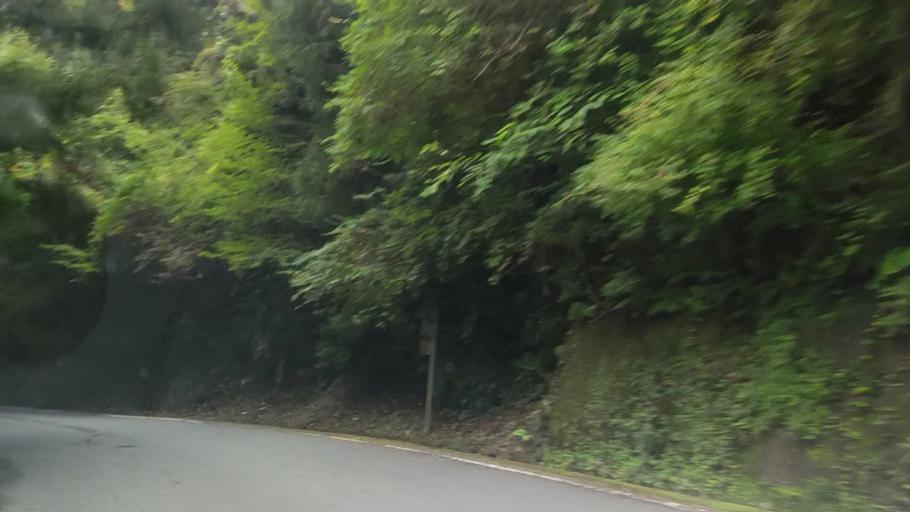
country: JP
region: Wakayama
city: Koya
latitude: 34.2269
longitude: 135.5400
